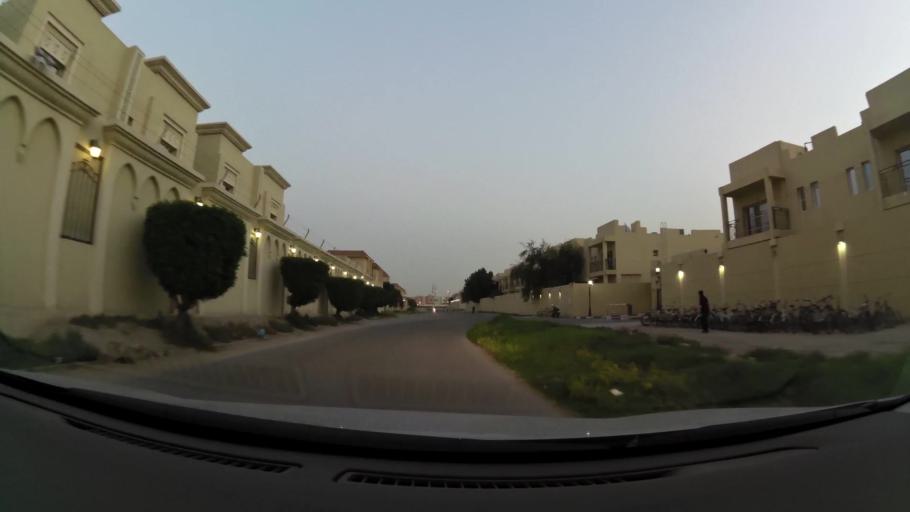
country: QA
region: Baladiyat ar Rayyan
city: Ar Rayyan
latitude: 25.2595
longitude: 51.4606
